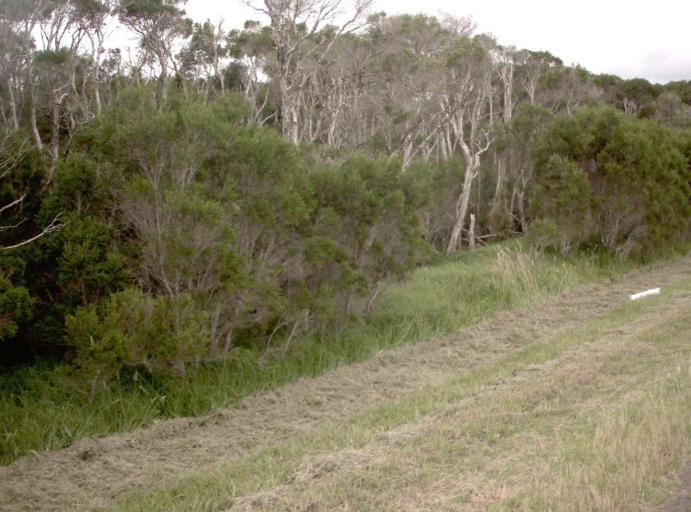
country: AU
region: Victoria
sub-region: Bass Coast
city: North Wonthaggi
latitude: -38.5836
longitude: 145.6203
